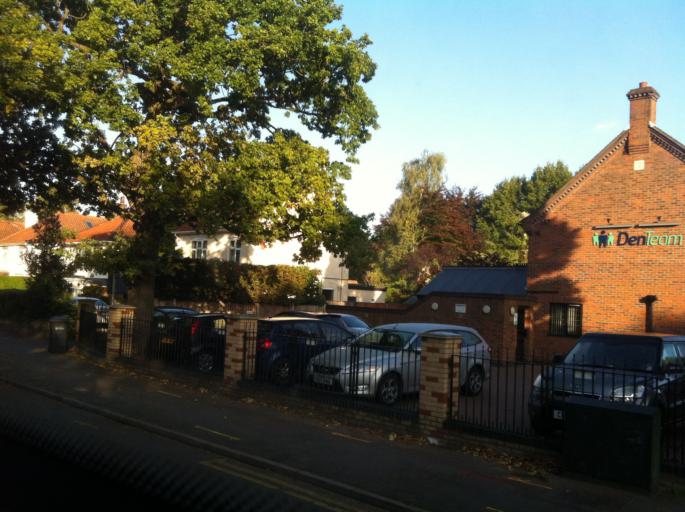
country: GB
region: England
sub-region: Norfolk
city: Cringleford
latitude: 52.6292
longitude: 1.2546
